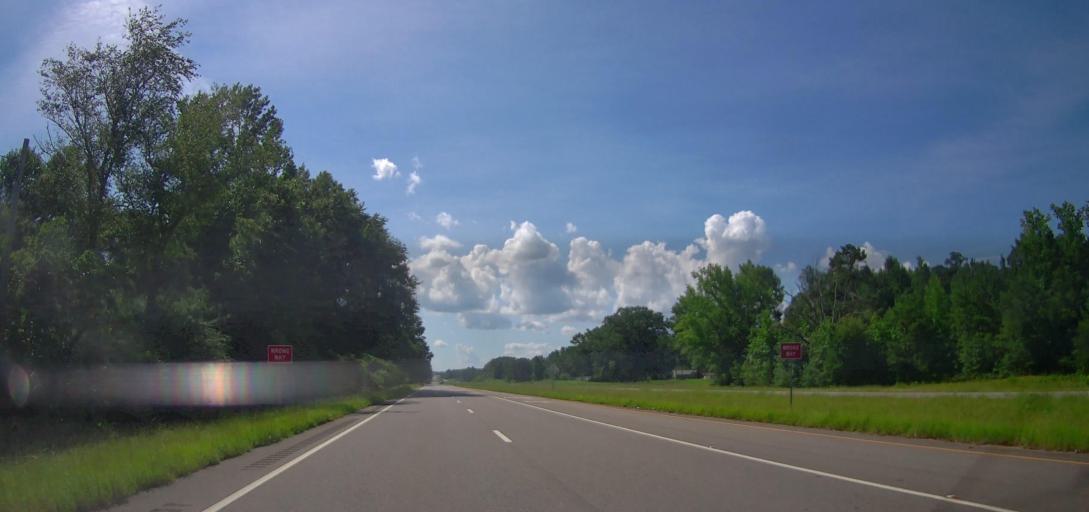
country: US
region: Alabama
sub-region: Pickens County
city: Gordo
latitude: 33.3404
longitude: -87.9394
